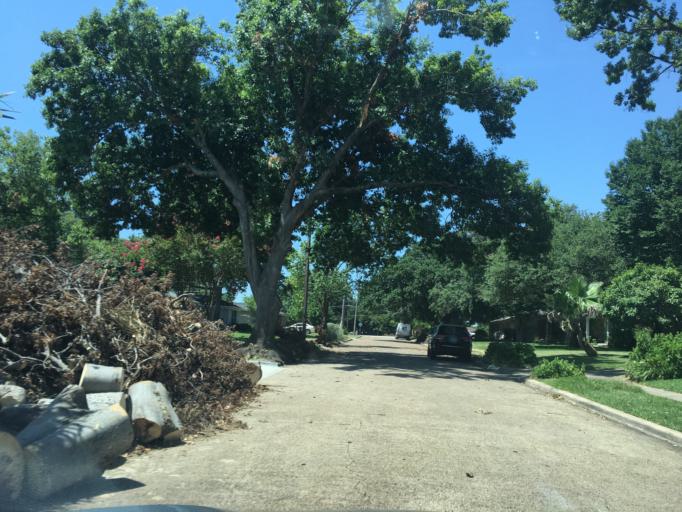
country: US
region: Texas
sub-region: Dallas County
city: Highland Park
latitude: 32.8512
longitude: -96.7454
